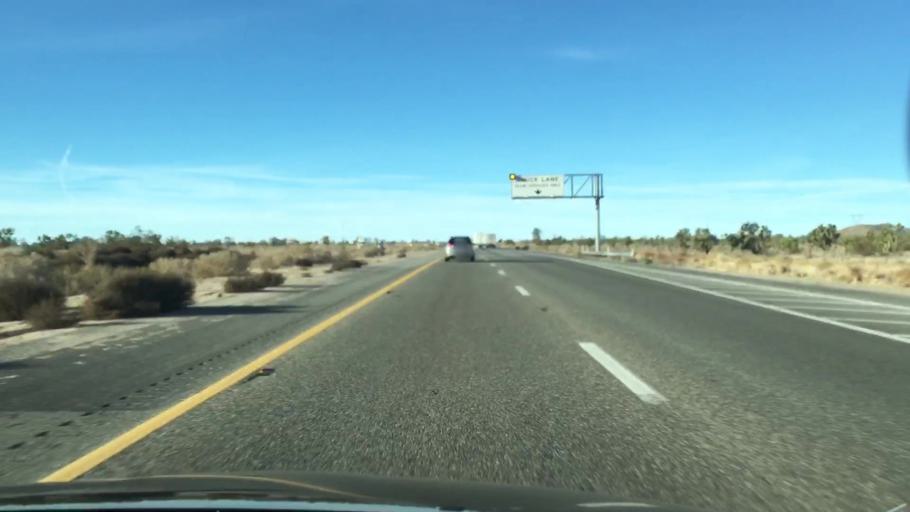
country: US
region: Nevada
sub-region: Clark County
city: Sandy Valley
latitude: 35.4075
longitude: -115.7783
